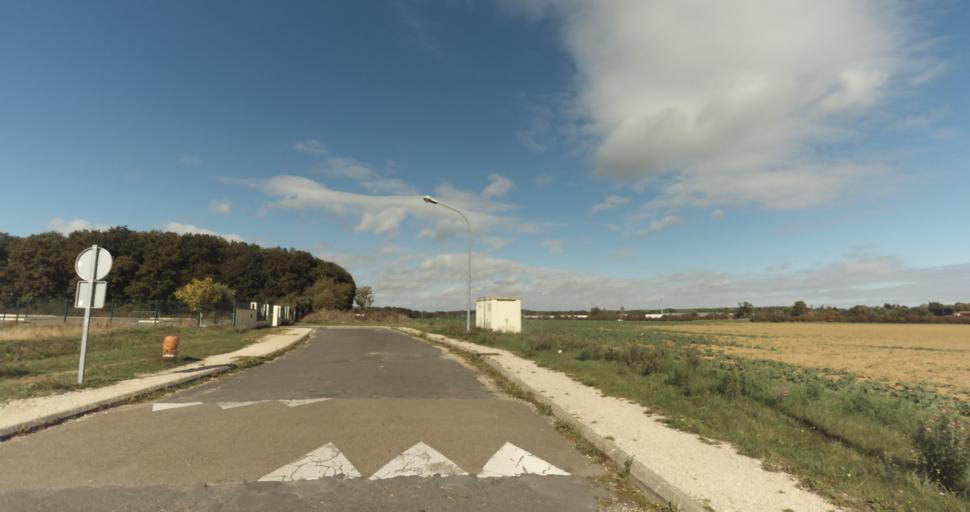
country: FR
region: Centre
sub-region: Departement d'Eure-et-Loir
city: Garnay
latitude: 48.7352
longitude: 1.3349
